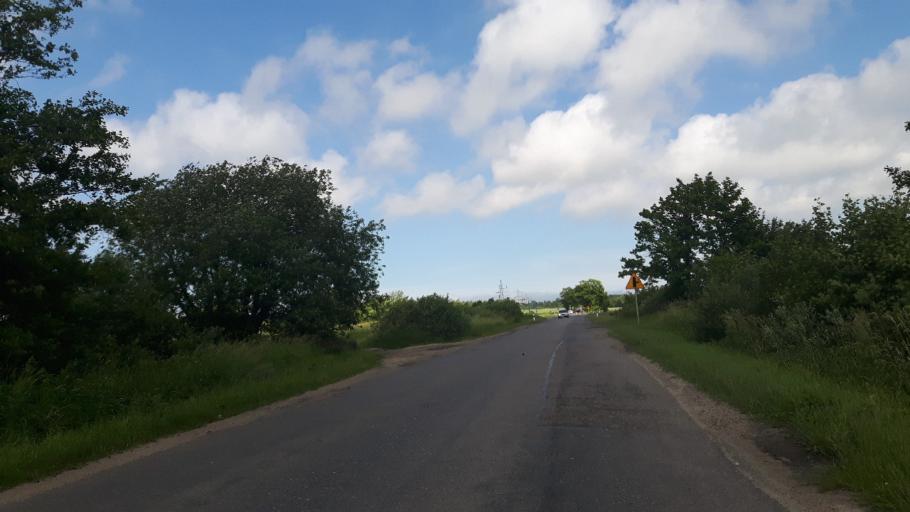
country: PL
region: Pomeranian Voivodeship
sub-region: Powiat slupski
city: Ustka
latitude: 54.5518
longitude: 16.8356
